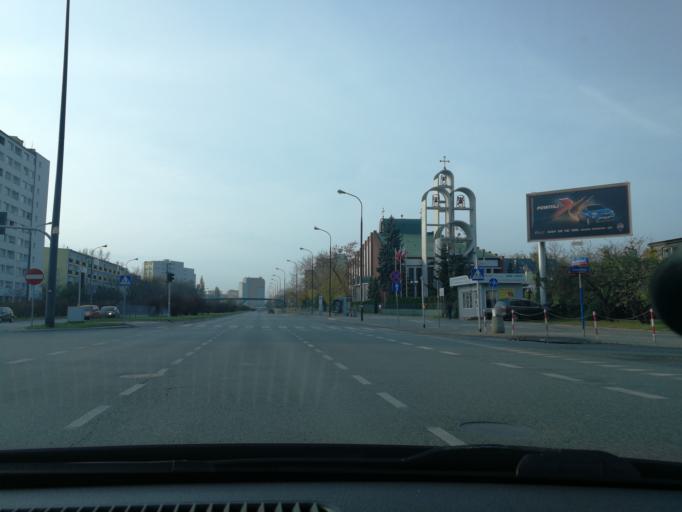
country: PL
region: Masovian Voivodeship
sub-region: Warszawa
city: Praga Poludnie
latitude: 52.2405
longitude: 21.0822
